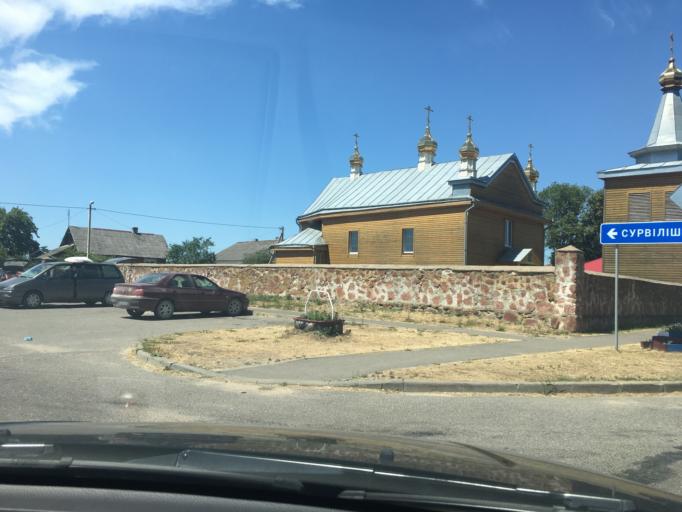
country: BY
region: Grodnenskaya
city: Hal'shany
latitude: 54.1583
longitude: 25.9068
